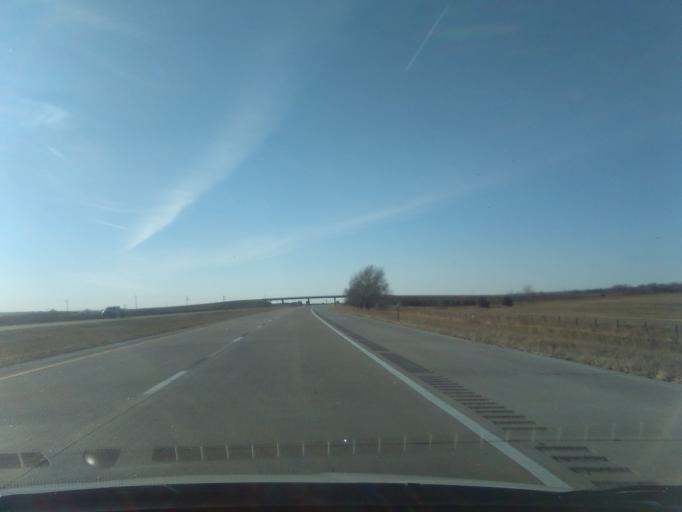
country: US
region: Nebraska
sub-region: Keith County
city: Ogallala
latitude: 41.0644
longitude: -101.9827
